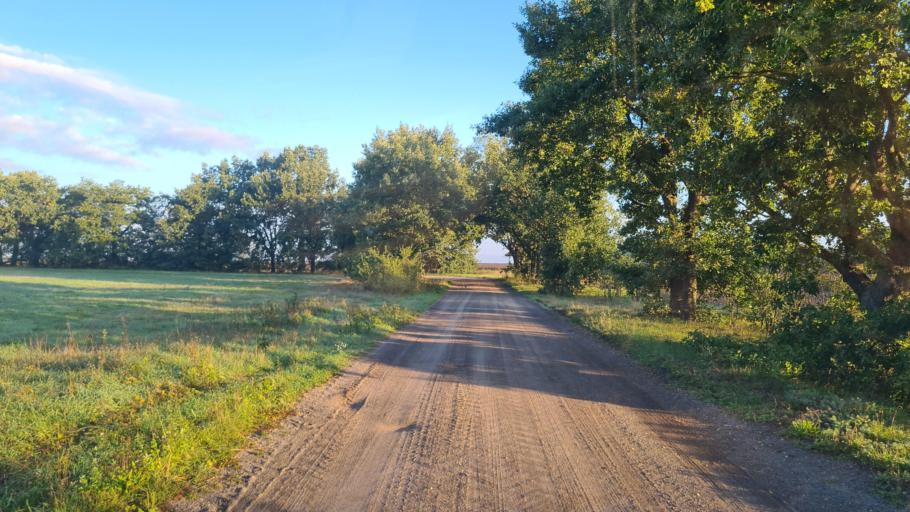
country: DE
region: Saxony-Anhalt
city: Holzdorf
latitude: 51.8081
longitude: 13.1157
